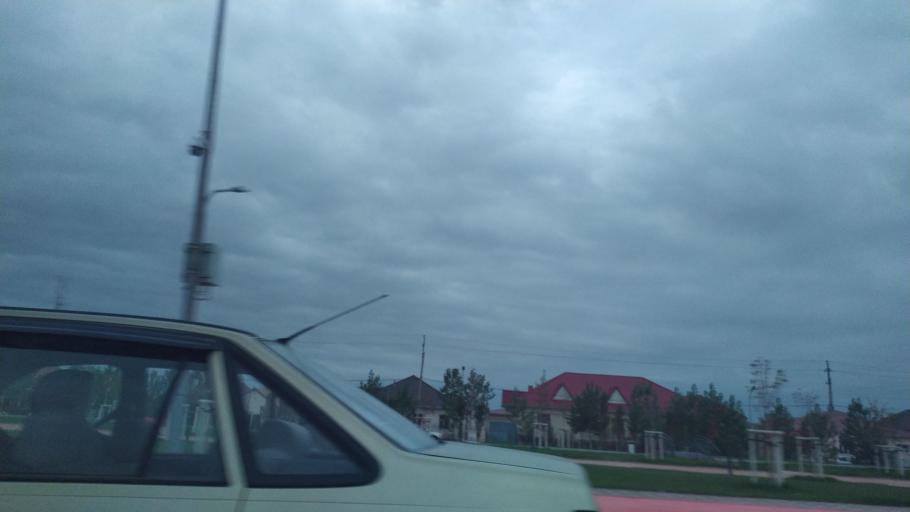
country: KZ
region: Ongtustik Qazaqstan
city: Turkestan
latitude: 43.2796
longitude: 68.3231
